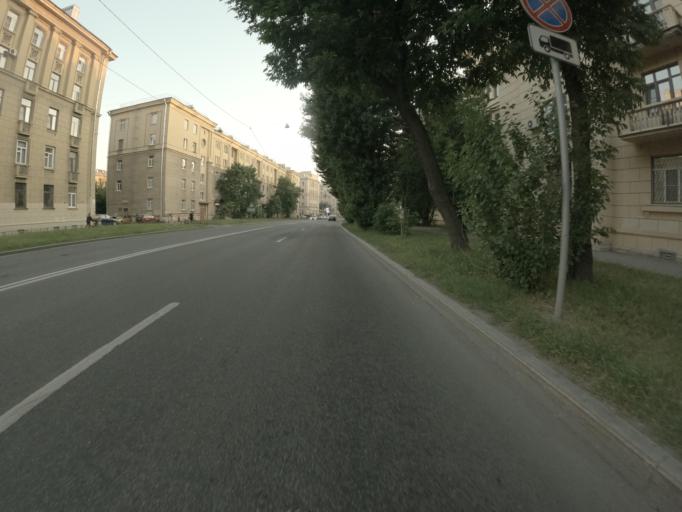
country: RU
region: St.-Petersburg
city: Avtovo
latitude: 59.8708
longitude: 30.2630
